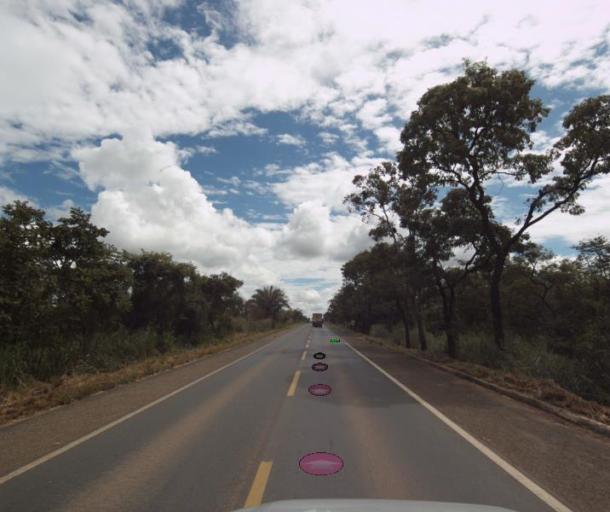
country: BR
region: Goias
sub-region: Uruacu
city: Uruacu
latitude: -14.4523
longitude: -49.1564
